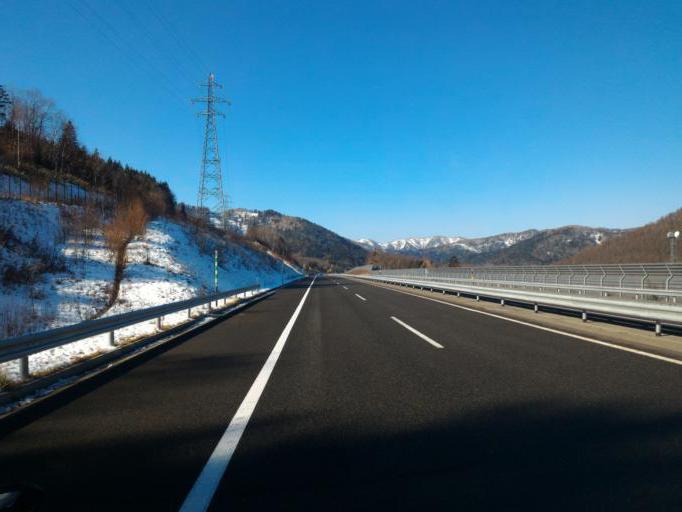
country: JP
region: Hokkaido
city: Shimo-furano
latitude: 43.0537
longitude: 142.5776
